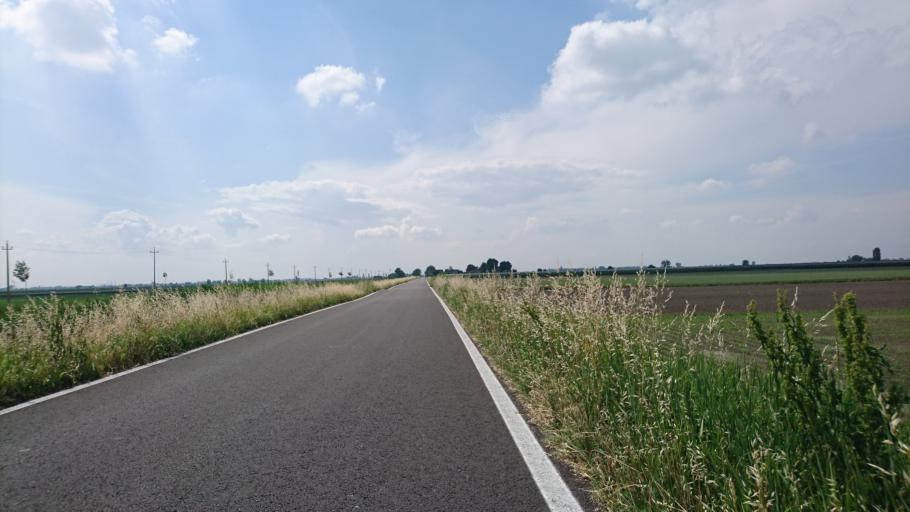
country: IT
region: Veneto
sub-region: Provincia di Verona
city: Castagnaro
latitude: 45.0717
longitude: 11.3952
